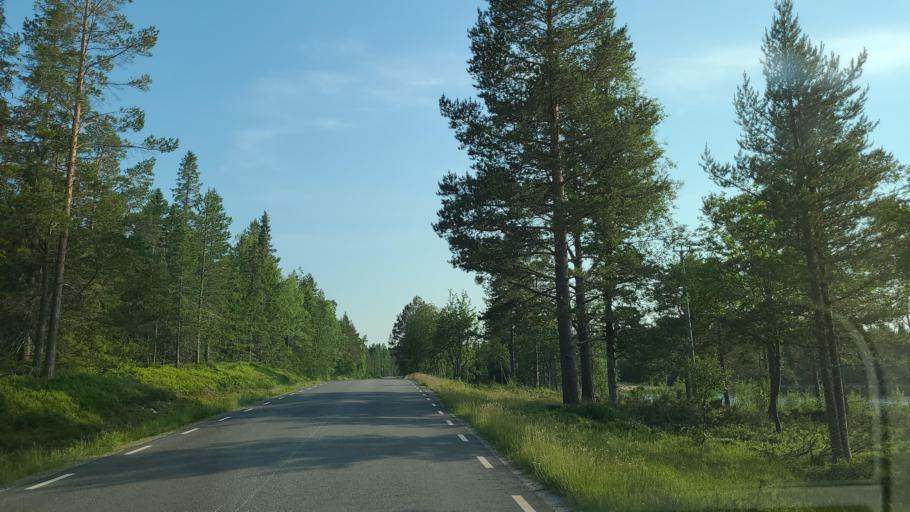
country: SE
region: Vaesterbotten
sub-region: Skelleftea Kommun
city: Burea
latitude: 64.4584
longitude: 21.5823
